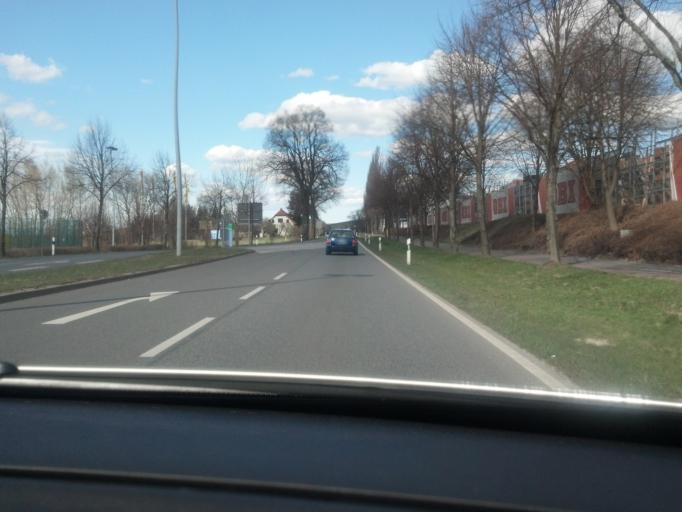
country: DE
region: Mecklenburg-Vorpommern
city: Neubrandenburg
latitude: 53.5863
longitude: 13.2723
